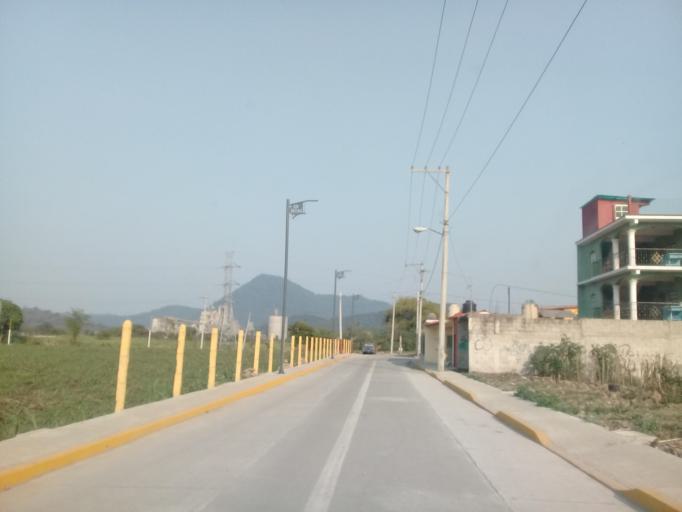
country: MX
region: Veracruz
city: Ixtac Zoquitlan
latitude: 18.8563
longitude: -97.0543
